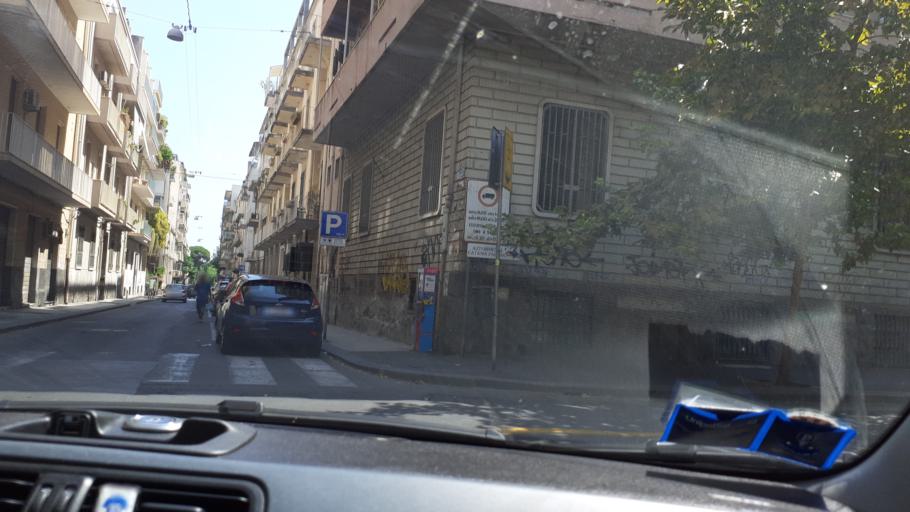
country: IT
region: Sicily
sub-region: Catania
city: Catania
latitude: 37.5099
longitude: 15.0790
